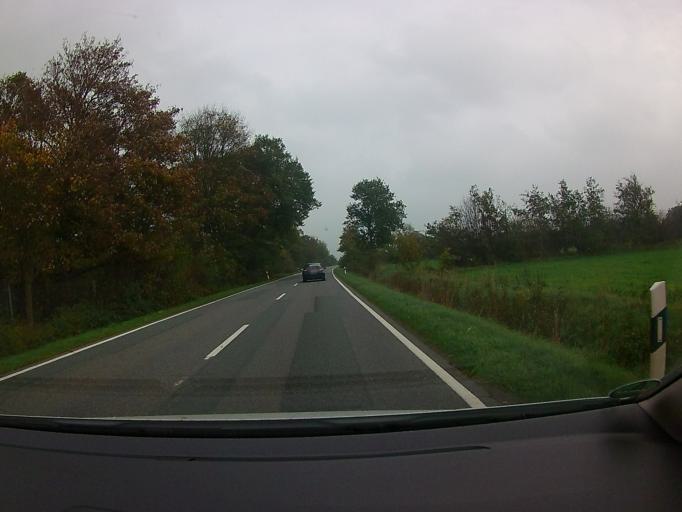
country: DE
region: Schleswig-Holstein
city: Grossenwiehe
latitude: 54.6959
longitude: 9.2539
